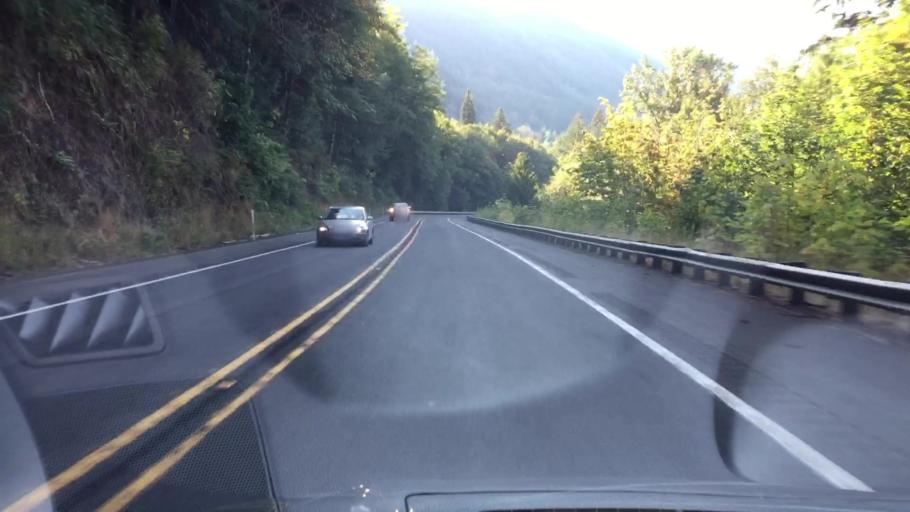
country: US
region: Washington
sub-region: Lewis County
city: Morton
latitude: 46.5211
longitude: -122.2216
